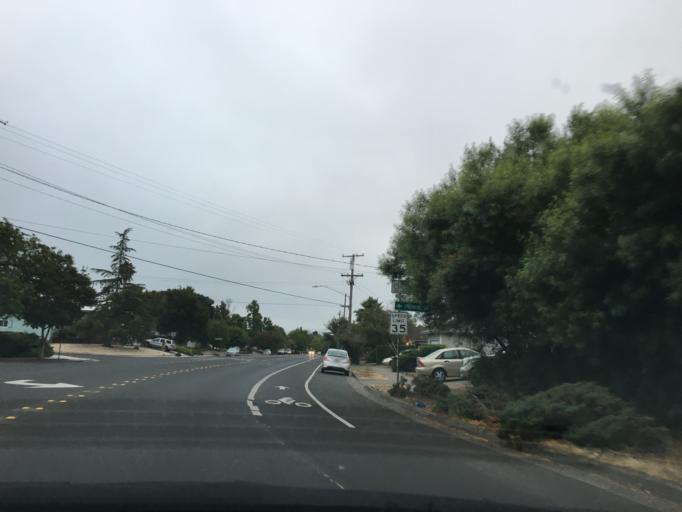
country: US
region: California
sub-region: Sonoma County
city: Santa Rosa
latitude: 38.4718
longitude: -122.6769
